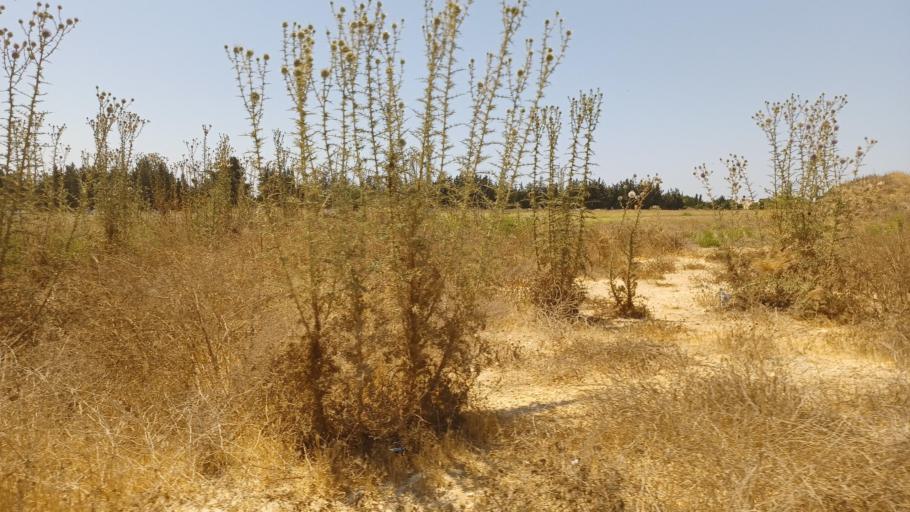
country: CY
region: Pafos
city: Paphos
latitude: 34.7600
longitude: 32.4417
